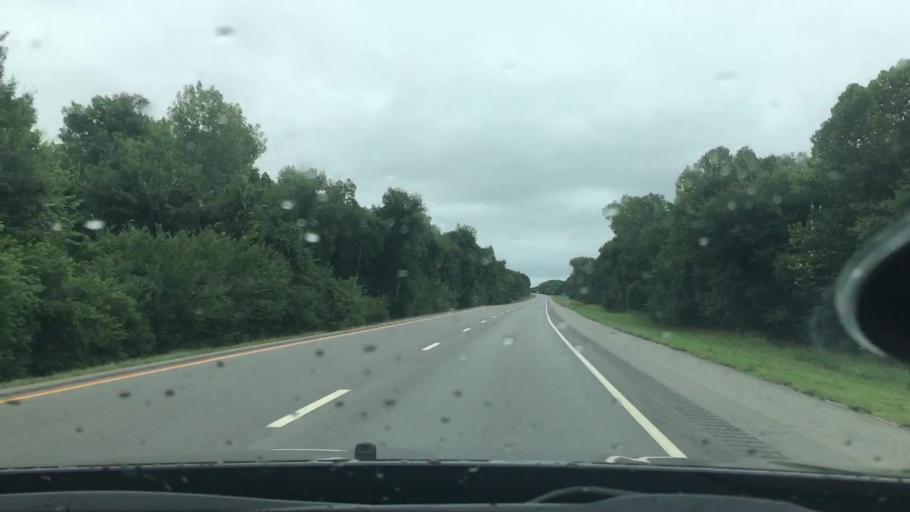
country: US
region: Oklahoma
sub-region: Okmulgee County
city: Morris
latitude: 35.4496
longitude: -95.7497
